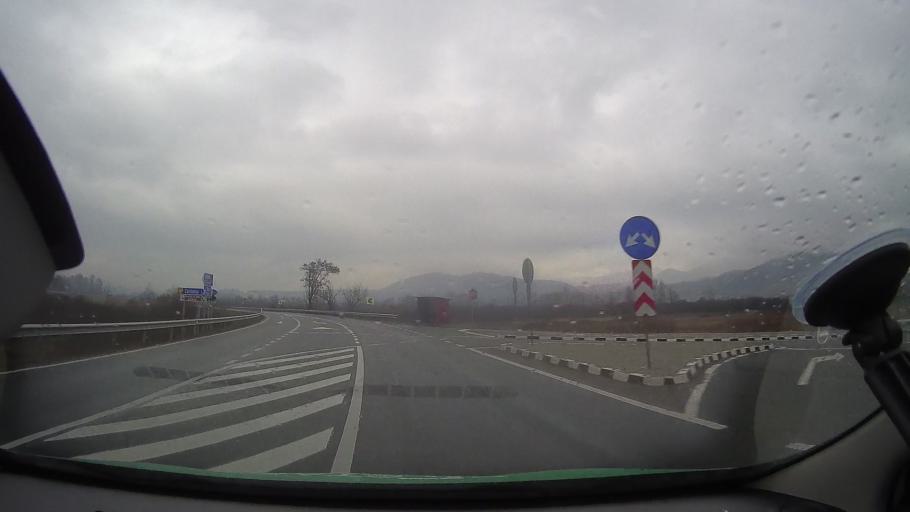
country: RO
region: Hunedoara
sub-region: Comuna Tomesti
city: Tomesti
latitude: 46.1805
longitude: 22.6617
